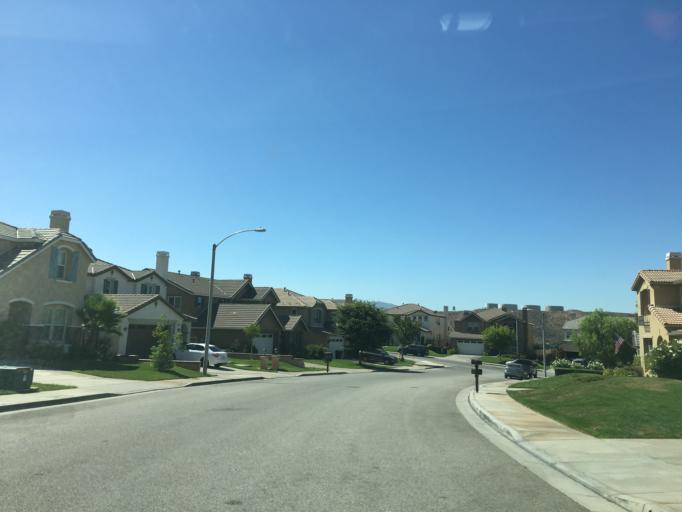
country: US
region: California
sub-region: Los Angeles County
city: Santa Clarita
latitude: 34.4487
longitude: -118.4788
